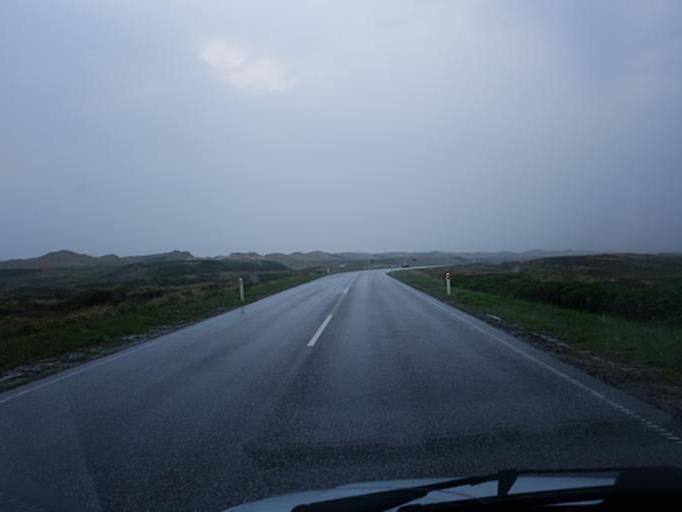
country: DK
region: Central Jutland
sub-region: Ringkobing-Skjern Kommune
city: Hvide Sande
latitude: 55.8252
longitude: 8.1752
